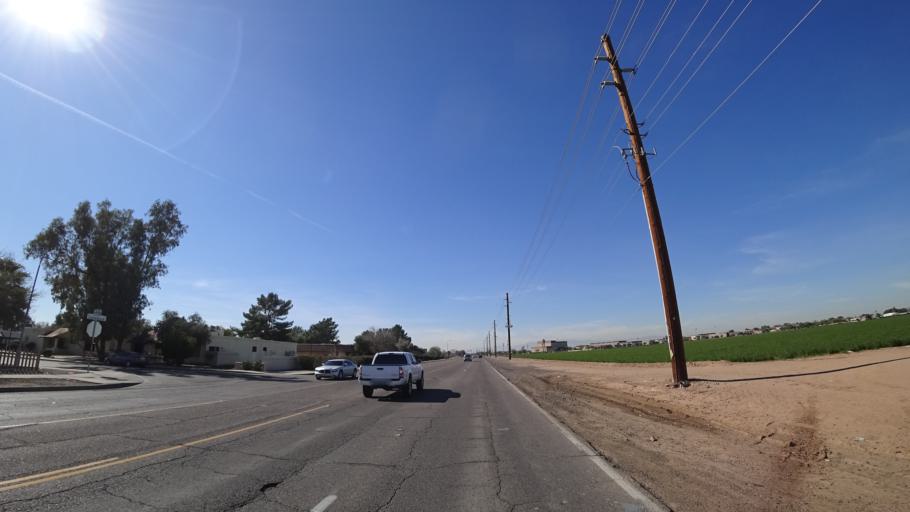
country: US
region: Arizona
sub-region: Maricopa County
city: Tolleson
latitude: 33.5089
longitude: -112.2503
